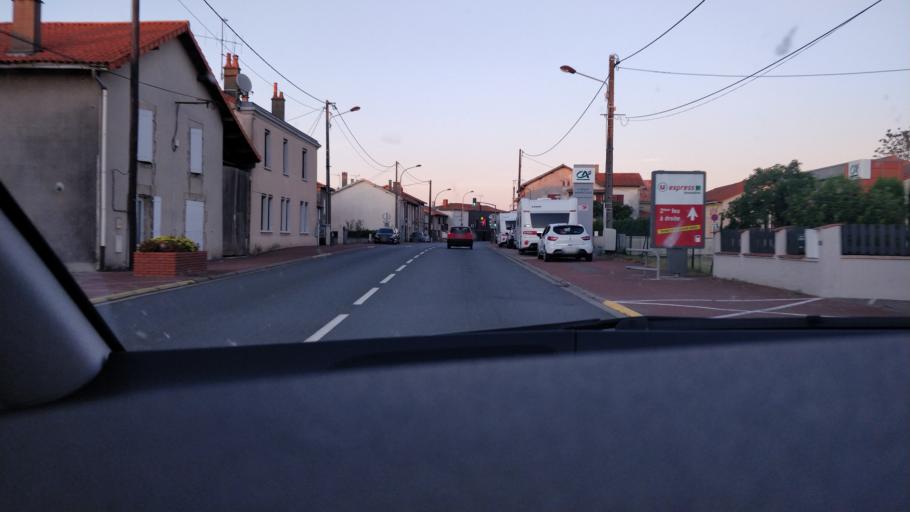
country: FR
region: Poitou-Charentes
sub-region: Departement de la Charente
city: Loubert
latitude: 45.8858
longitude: 0.5780
